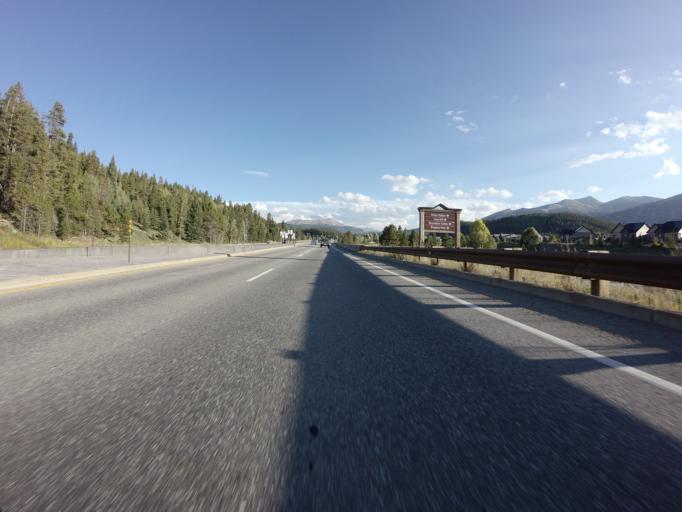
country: US
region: Colorado
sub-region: Summit County
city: Breckenridge
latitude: 39.5002
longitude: -106.0469
